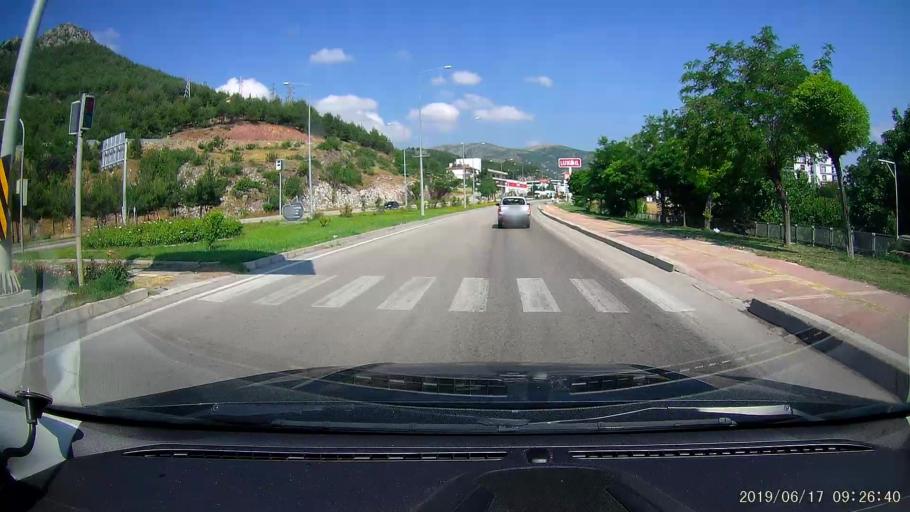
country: TR
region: Amasya
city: Amasya
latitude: 40.6706
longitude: 35.8332
